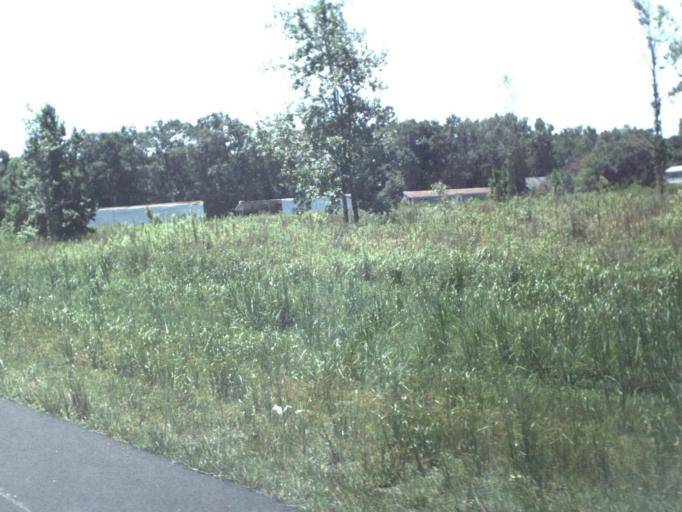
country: US
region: Florida
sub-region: Union County
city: Lake Butler
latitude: 29.9114
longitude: -82.4233
